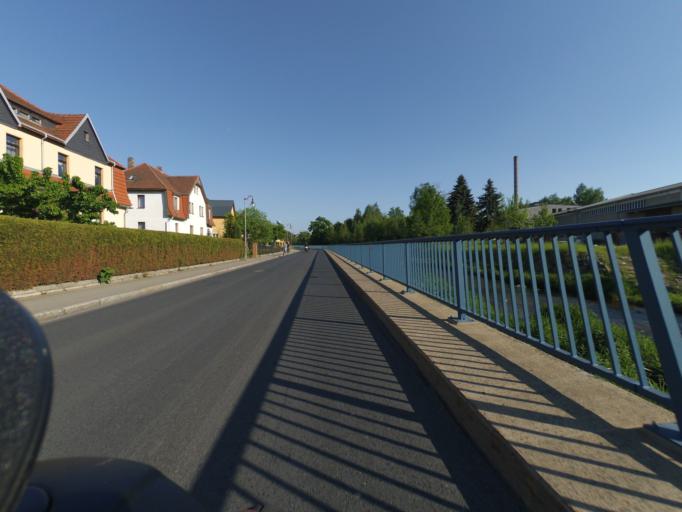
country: DE
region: Saxony
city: Dippoldiswalde
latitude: 50.8960
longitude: 13.6624
